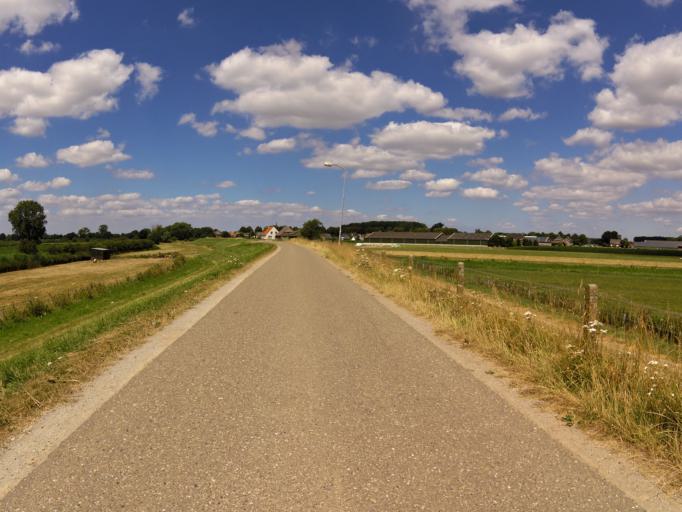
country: NL
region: Gelderland
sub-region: Gemeente Maasdriel
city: Heerewaarden
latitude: 51.7815
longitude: 5.3505
